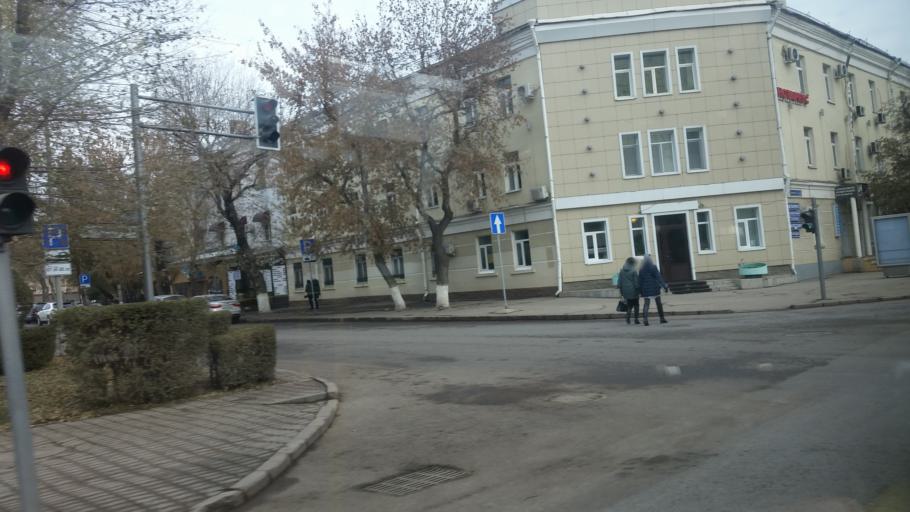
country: KZ
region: Astana Qalasy
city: Astana
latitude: 51.1653
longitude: 71.4248
